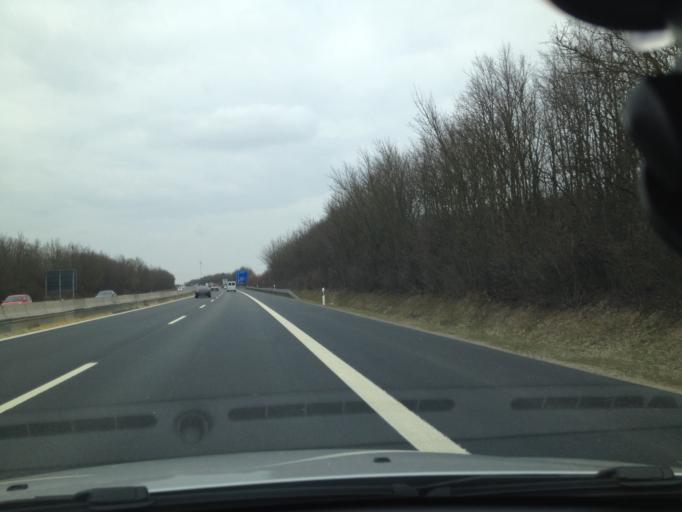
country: DE
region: Bavaria
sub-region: Regierungsbezirk Unterfranken
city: Biebelried
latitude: 49.7512
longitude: 10.1075
